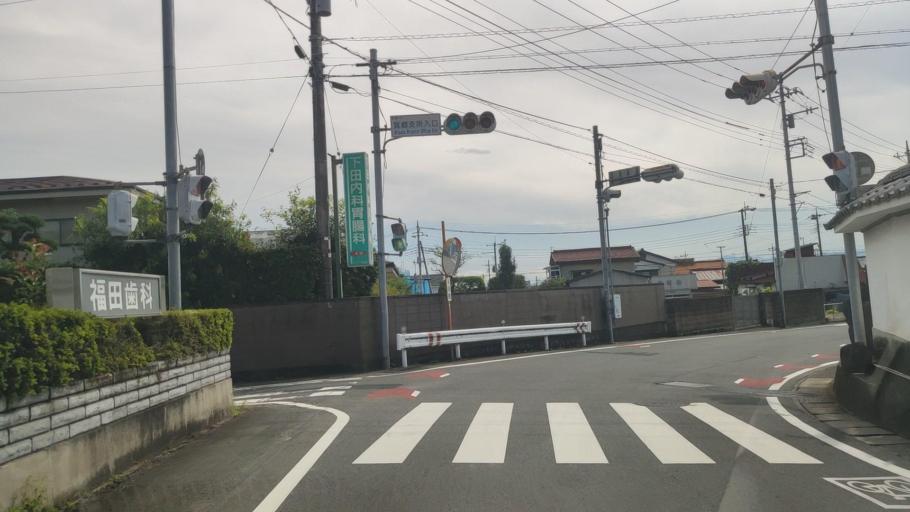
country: JP
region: Gunma
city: Kanekomachi
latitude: 36.3915
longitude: 138.9580
